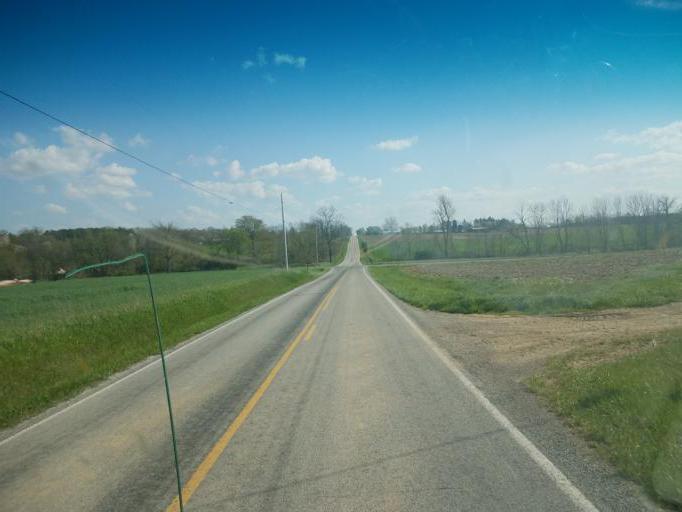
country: US
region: Ohio
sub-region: Wayne County
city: Creston
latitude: 40.9598
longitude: -81.9572
